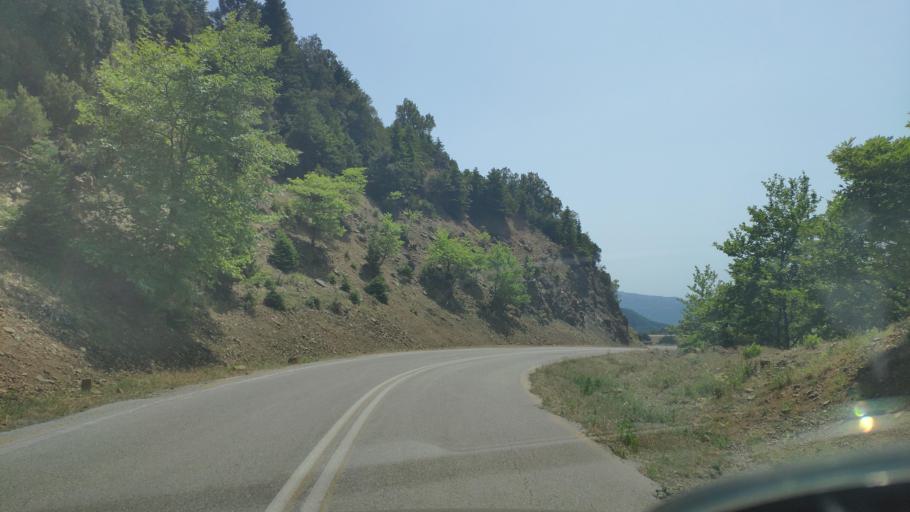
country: GR
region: Epirus
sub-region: Nomos Artas
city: Ano Kalentini
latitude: 39.2367
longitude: 21.2279
